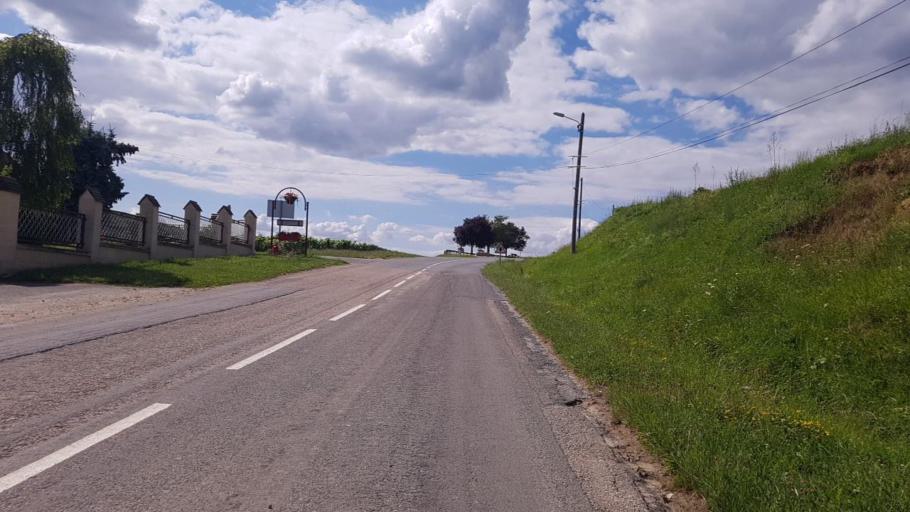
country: FR
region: Picardie
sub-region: Departement de l'Aisne
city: Crezancy
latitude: 49.0628
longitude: 3.5696
